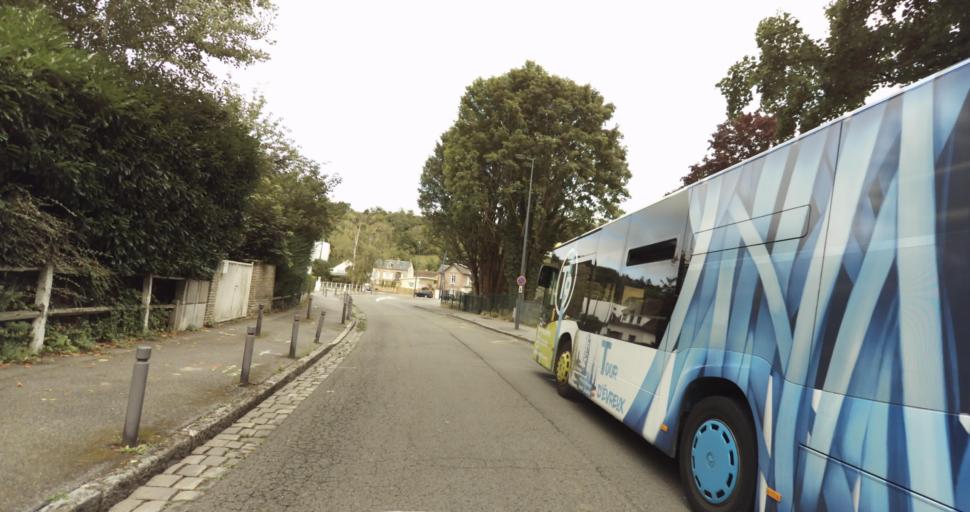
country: FR
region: Haute-Normandie
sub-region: Departement de l'Eure
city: Evreux
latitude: 49.0263
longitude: 1.1423
